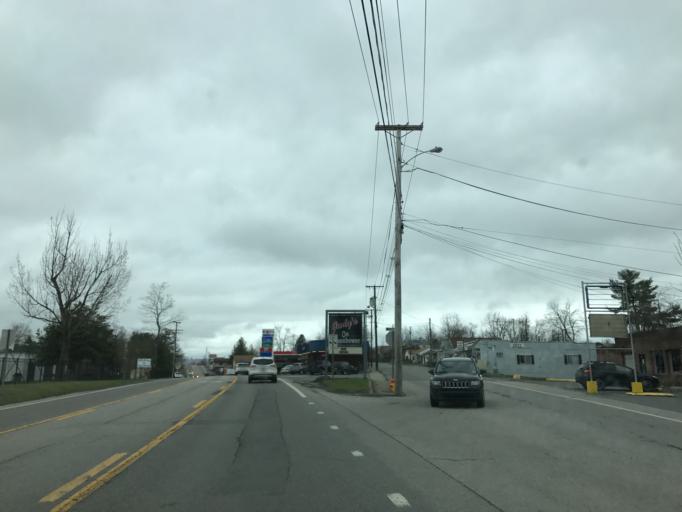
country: US
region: West Virginia
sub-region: Raleigh County
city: Beckley
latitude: 37.7862
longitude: -81.1716
